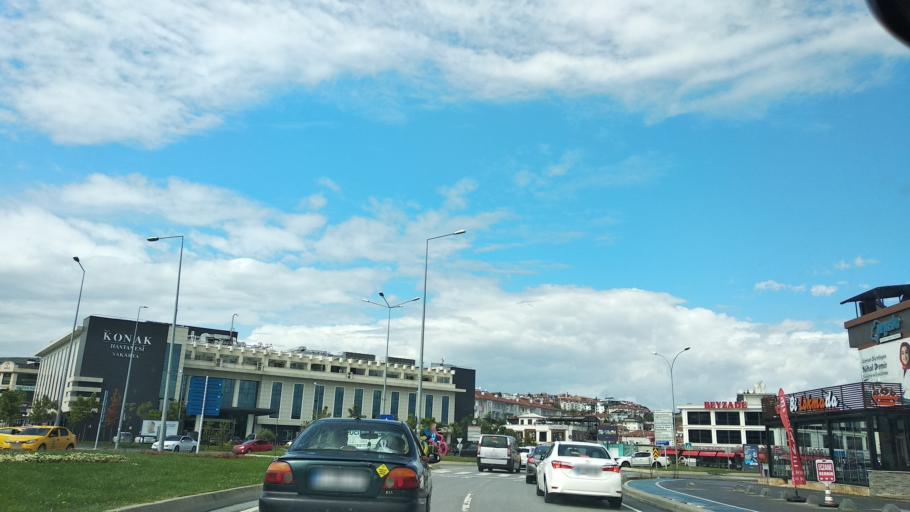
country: TR
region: Sakarya
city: Adapazari
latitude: 40.7602
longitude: 30.3636
